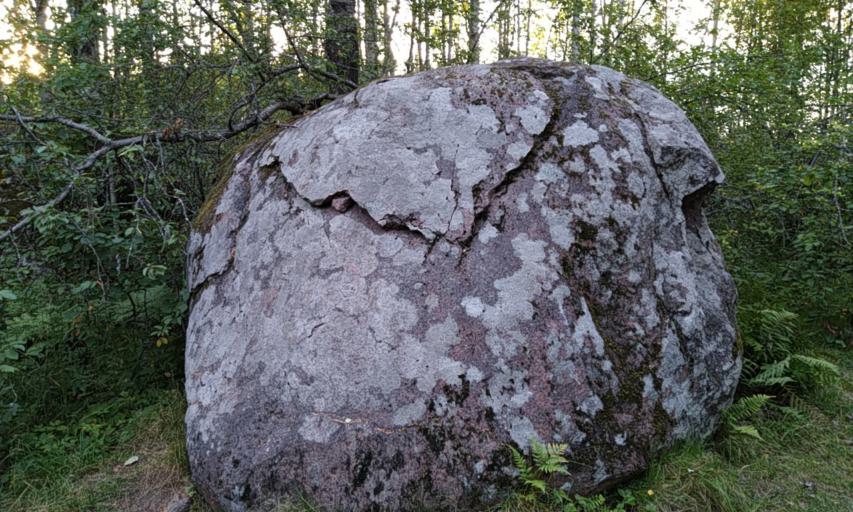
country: RU
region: Leningrad
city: Sapernoye
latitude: 60.8372
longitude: 29.8174
